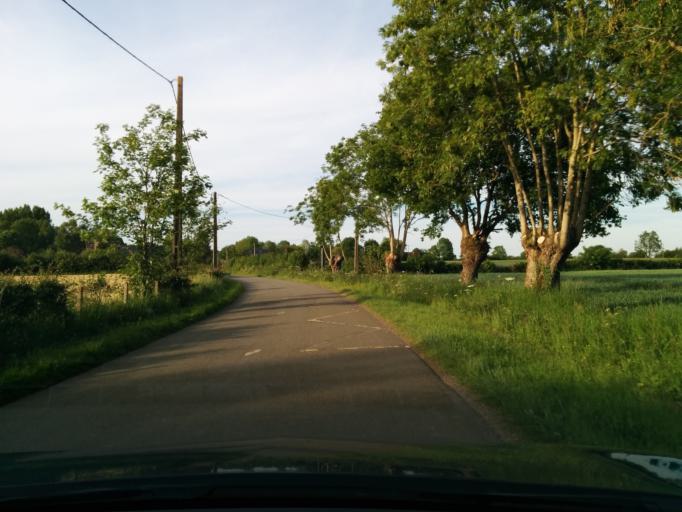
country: FR
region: Haute-Normandie
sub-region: Departement de la Seine-Maritime
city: Serqueux
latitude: 49.6722
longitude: 1.4793
